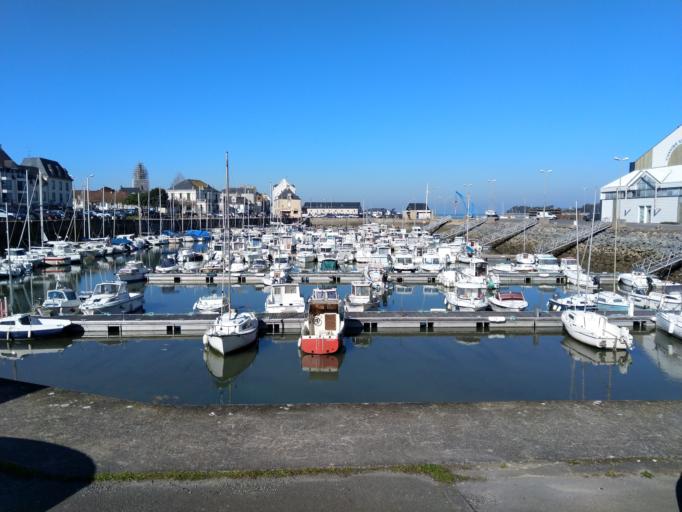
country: FR
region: Pays de la Loire
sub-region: Departement de la Loire-Atlantique
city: Le Croisic
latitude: 47.2922
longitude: -2.5072
